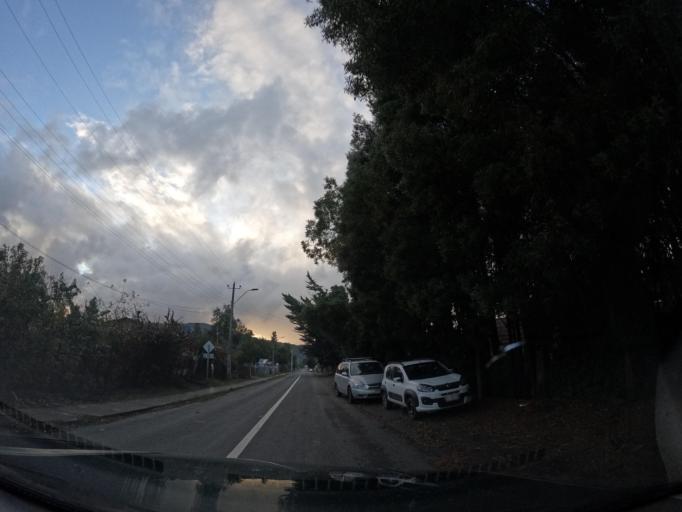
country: CL
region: Biobio
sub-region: Provincia de Concepcion
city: Chiguayante
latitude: -37.0563
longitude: -72.9579
